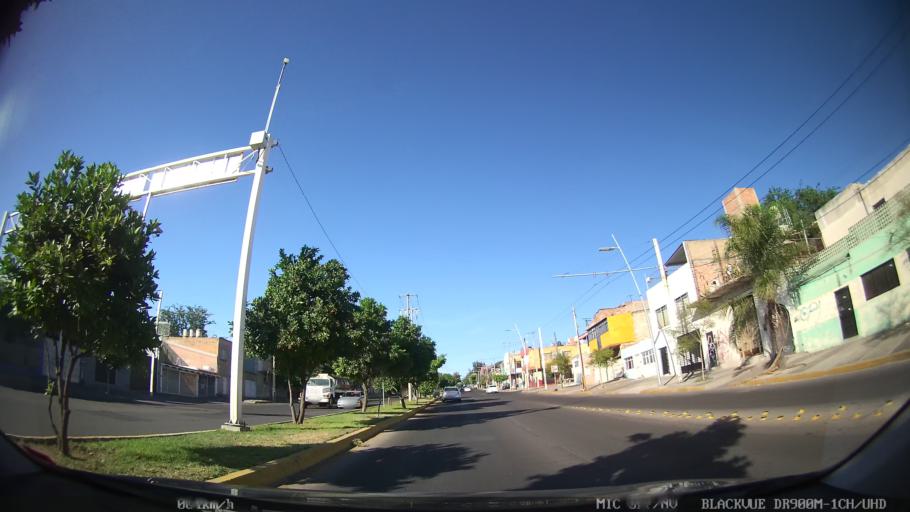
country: MX
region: Jalisco
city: Tlaquepaque
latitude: 20.6920
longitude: -103.3105
